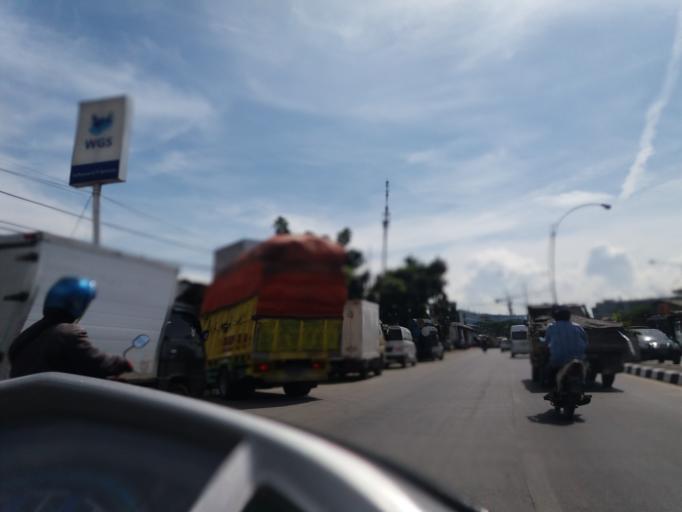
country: ID
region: West Java
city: Margahayukencana
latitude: -6.9358
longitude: 107.5785
